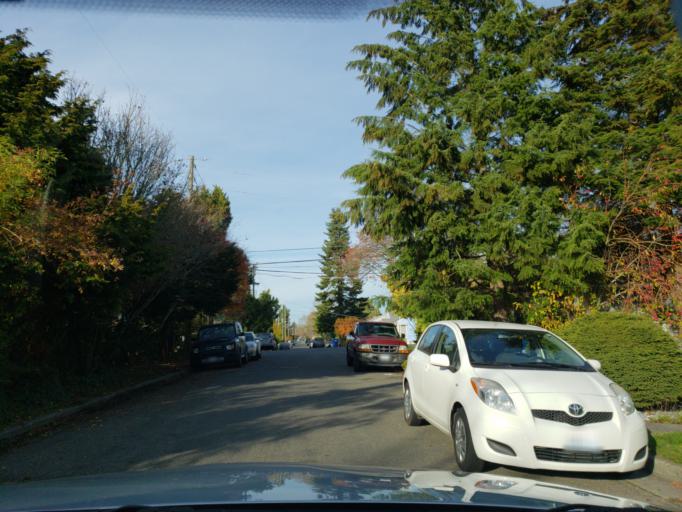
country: US
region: Washington
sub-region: King County
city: Shoreline
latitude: 47.6957
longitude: -122.3567
